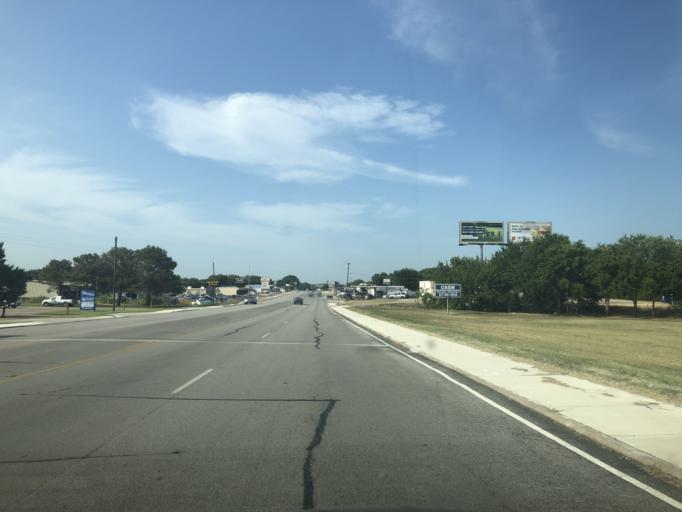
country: US
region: Texas
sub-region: Tarrant County
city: Benbrook
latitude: 32.7117
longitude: -97.4464
